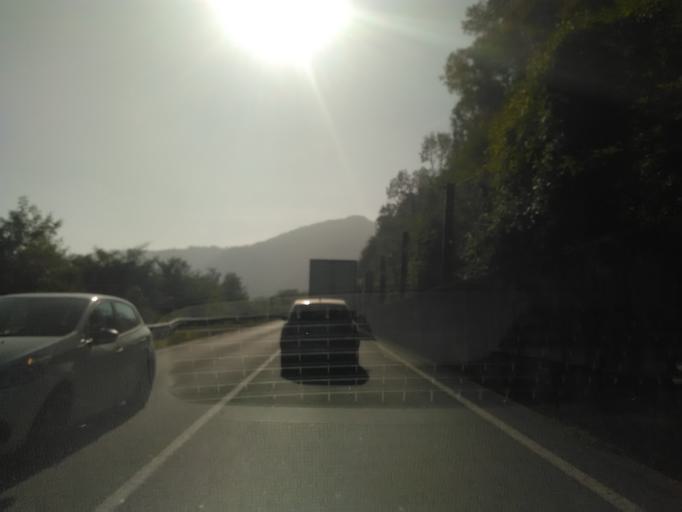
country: IT
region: Piedmont
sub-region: Provincia di Vercelli
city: Borgosesia
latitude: 45.7209
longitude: 8.2628
